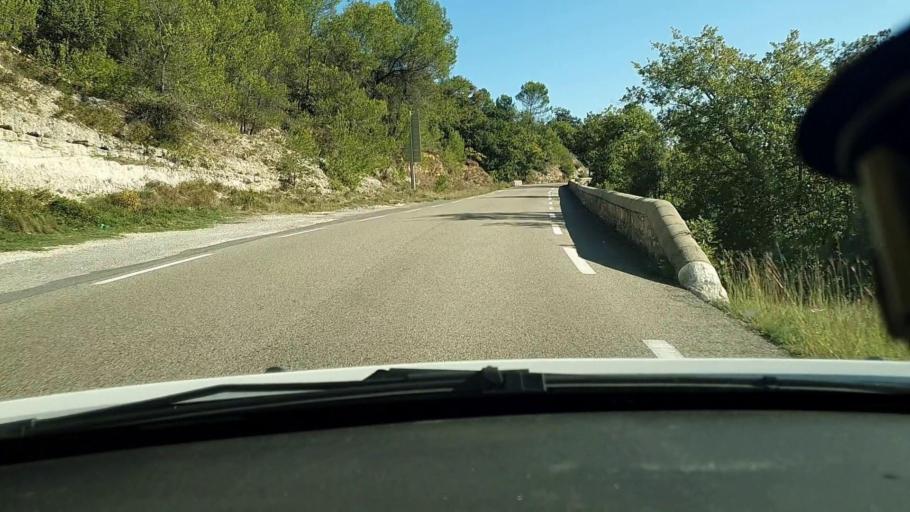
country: FR
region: Languedoc-Roussillon
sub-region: Departement du Gard
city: Goudargues
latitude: 44.2730
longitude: 4.4404
